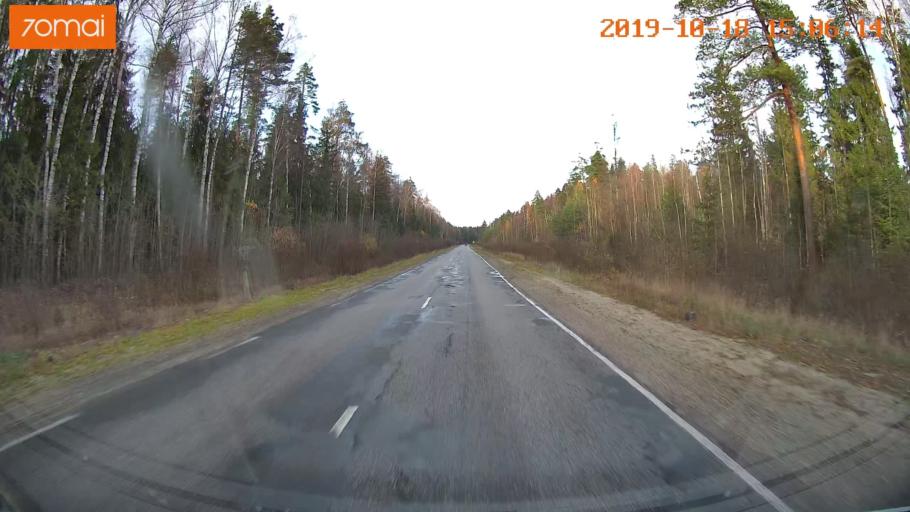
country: RU
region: Vladimir
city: Gus'-Khrustal'nyy
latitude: 55.5269
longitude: 40.5771
